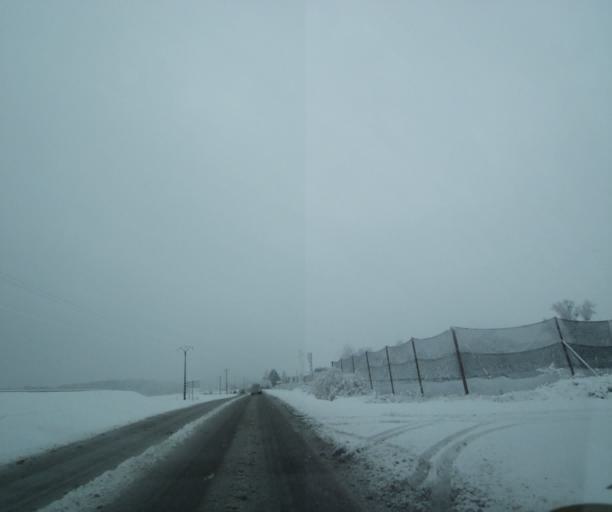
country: FR
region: Champagne-Ardenne
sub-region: Departement de la Haute-Marne
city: Saint-Dizier
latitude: 48.6191
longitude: 4.9224
